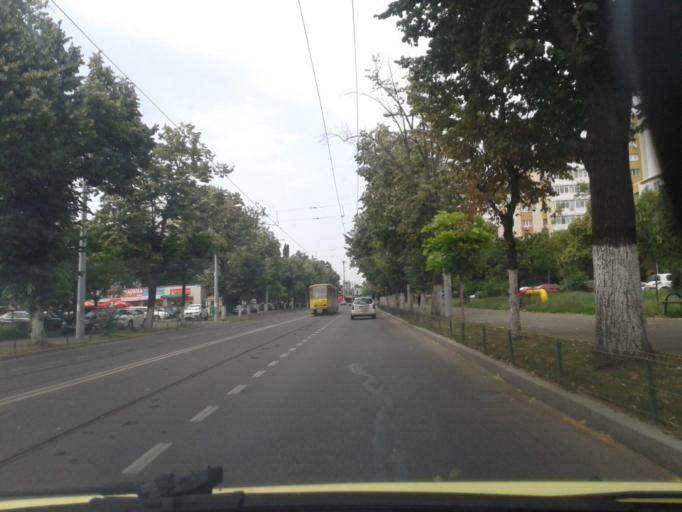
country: RO
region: Prahova
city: Ploiesti
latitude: 44.9444
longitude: 25.9931
